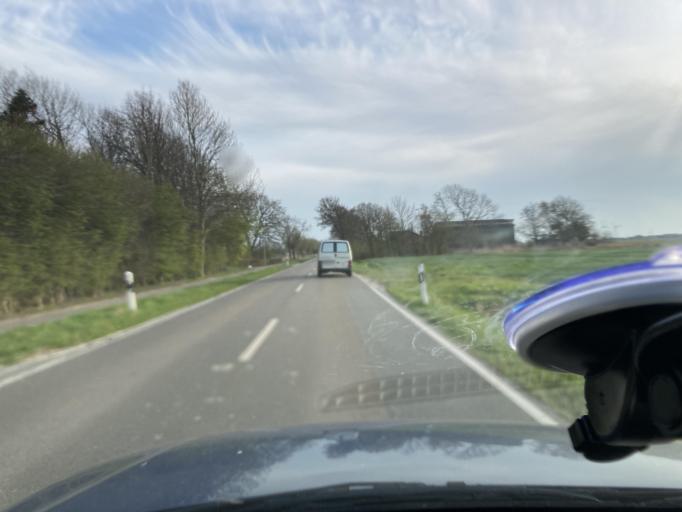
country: DE
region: Schleswig-Holstein
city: Wesselburen
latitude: 54.2275
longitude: 8.9303
